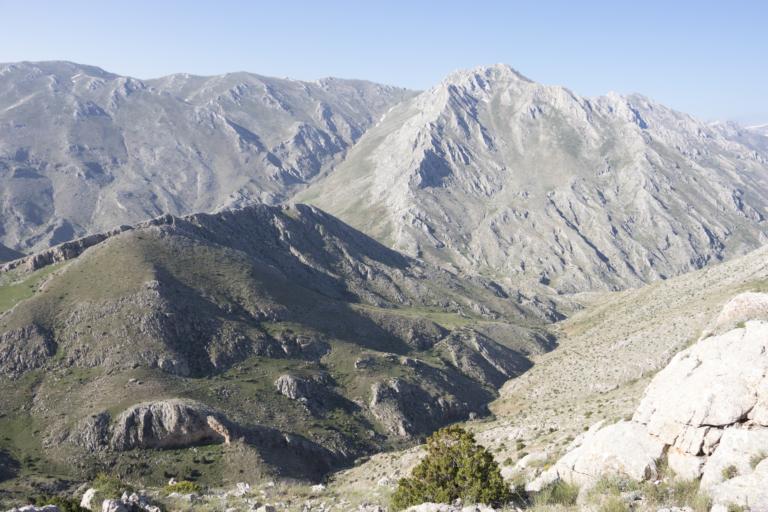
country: TR
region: Adana
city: Tufanbeyli
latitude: 38.3921
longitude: 36.1696
